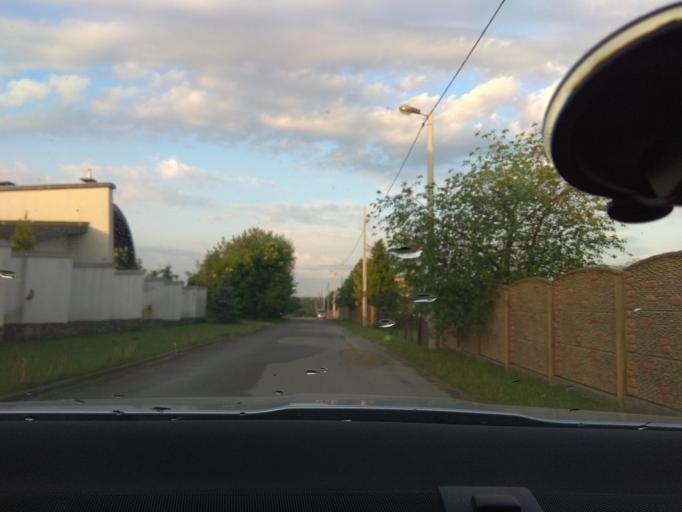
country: BY
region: Grodnenskaya
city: Hrodna
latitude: 53.6468
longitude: 23.7854
